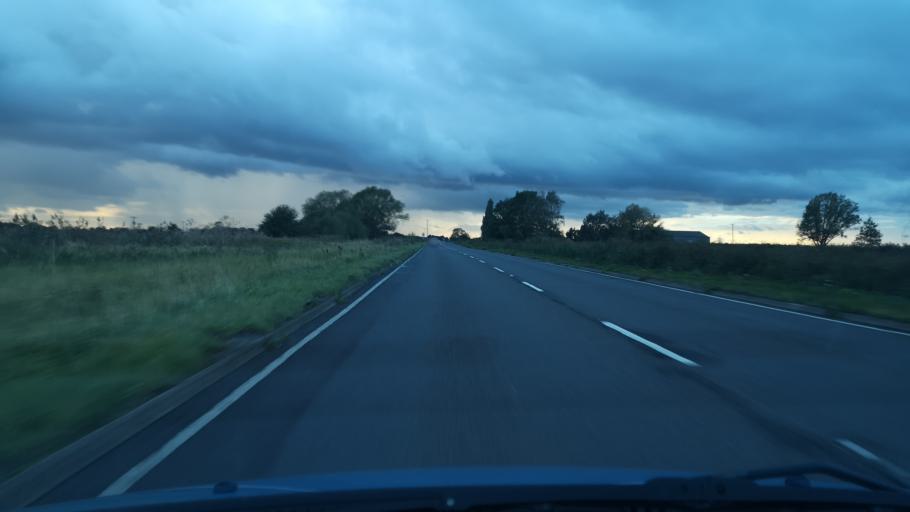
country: GB
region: England
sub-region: North Lincolnshire
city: Gunness
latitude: 53.5794
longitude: -0.7765
